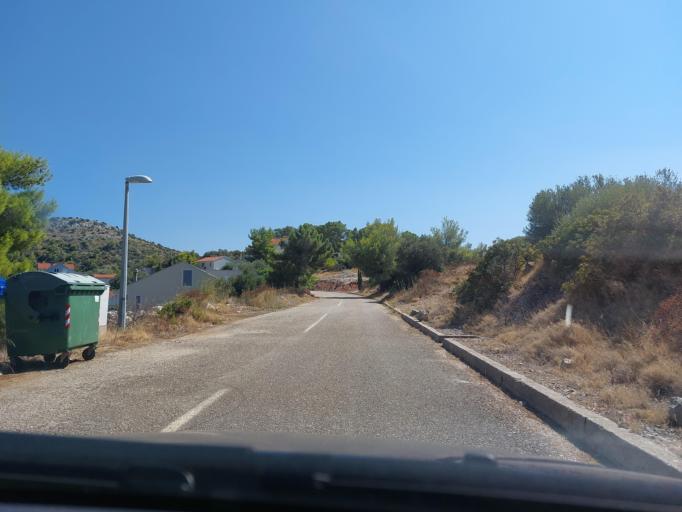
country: HR
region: Dubrovacko-Neretvanska
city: Smokvica
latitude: 42.7331
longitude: 16.8848
